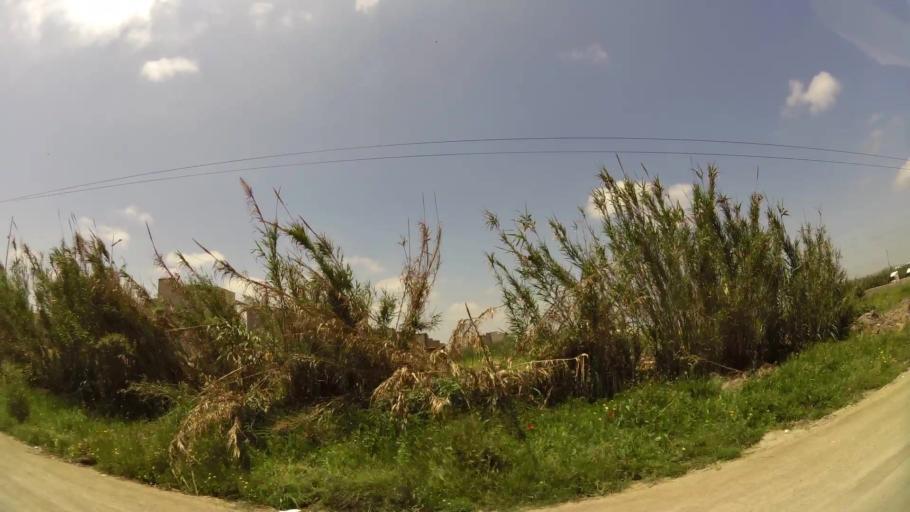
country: MA
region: Fes-Boulemane
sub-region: Fes
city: Fes
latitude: 34.0358
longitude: -5.0604
